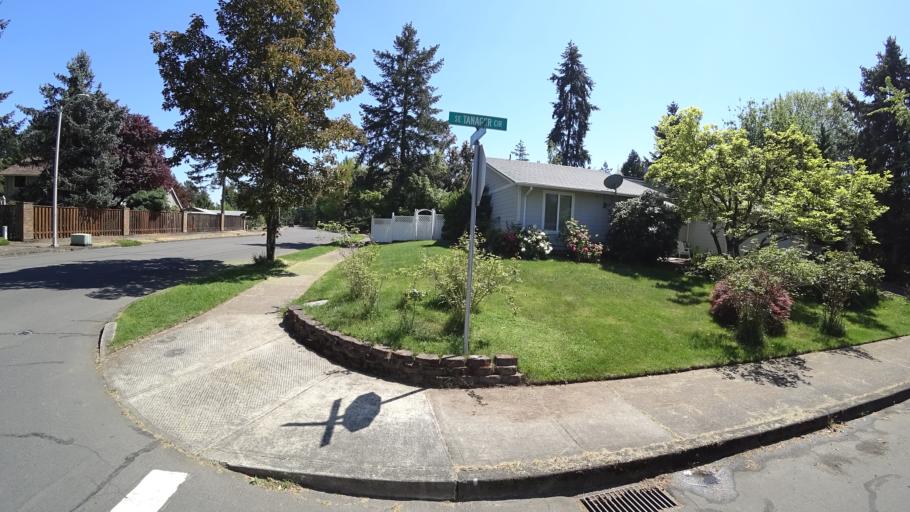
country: US
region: Oregon
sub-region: Washington County
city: Hillsboro
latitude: 45.4988
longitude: -122.9598
